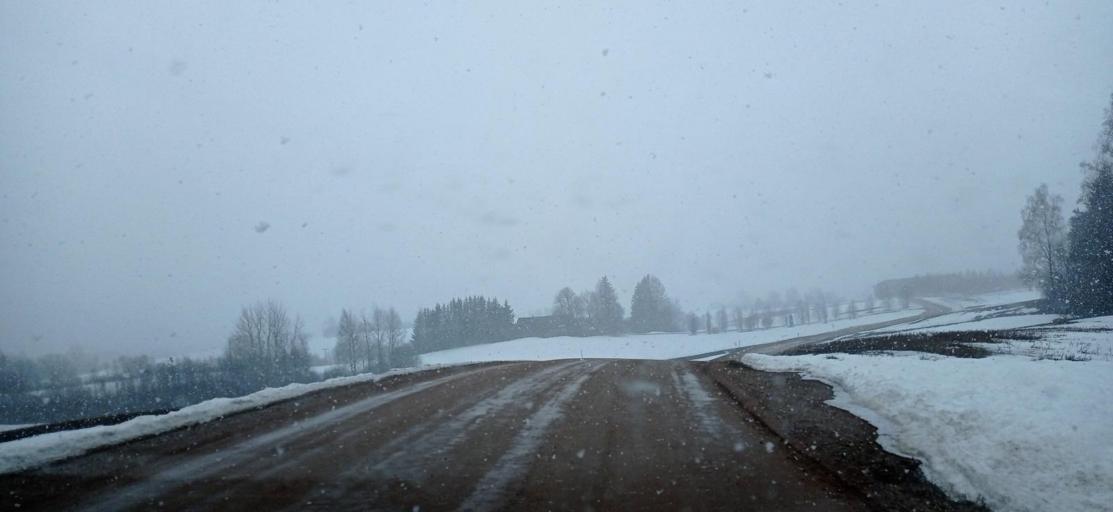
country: EE
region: Tartu
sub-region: Noo vald
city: Noo
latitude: 58.0935
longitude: 26.6689
